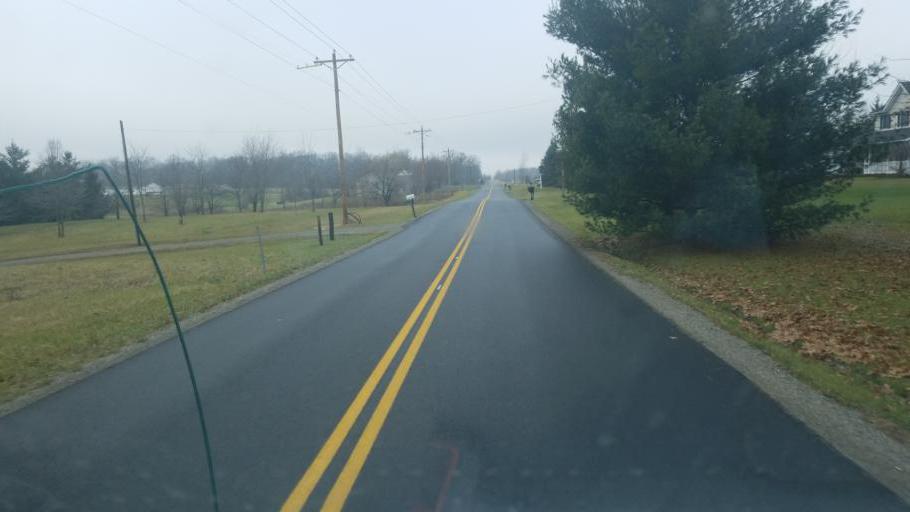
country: US
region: Ohio
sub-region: Champaign County
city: North Lewisburg
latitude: 40.2738
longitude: -83.5627
